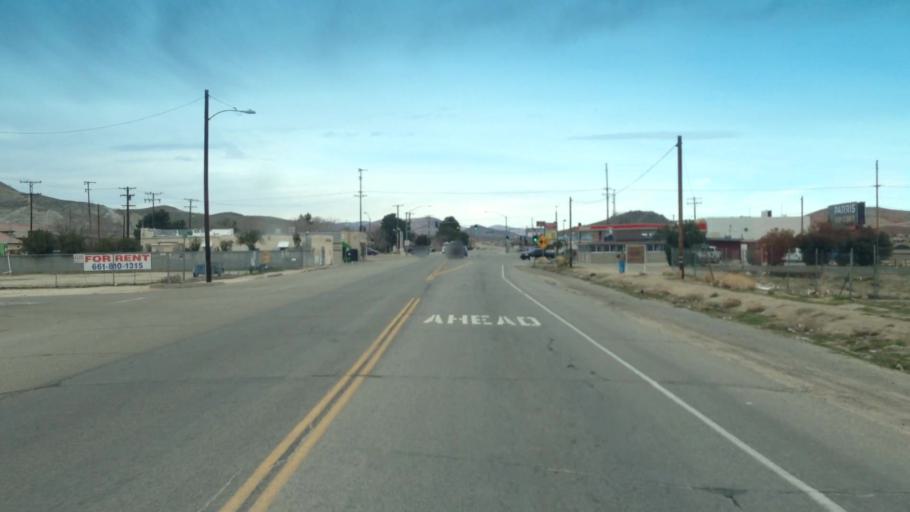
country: US
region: California
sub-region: Kern County
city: Rosamond
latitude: 34.8624
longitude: -118.1630
